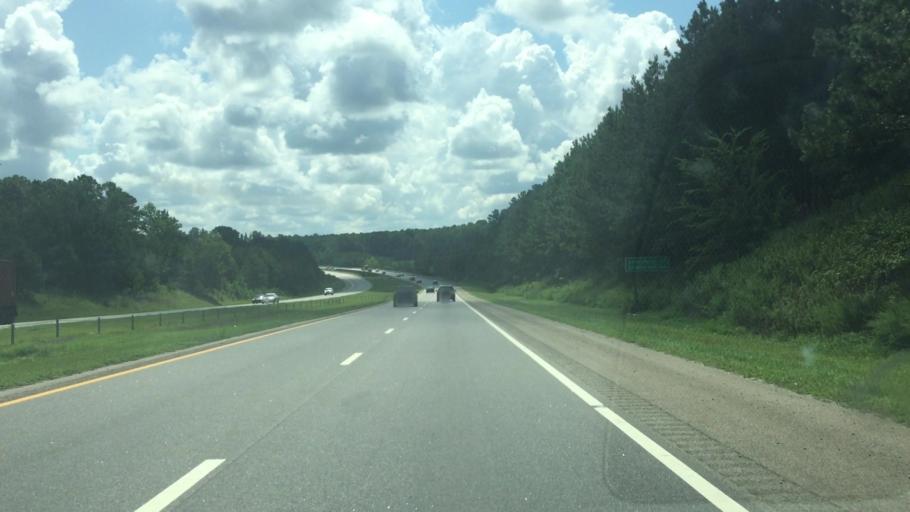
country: US
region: North Carolina
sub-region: Richmond County
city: Cordova
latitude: 34.9245
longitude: -79.8181
